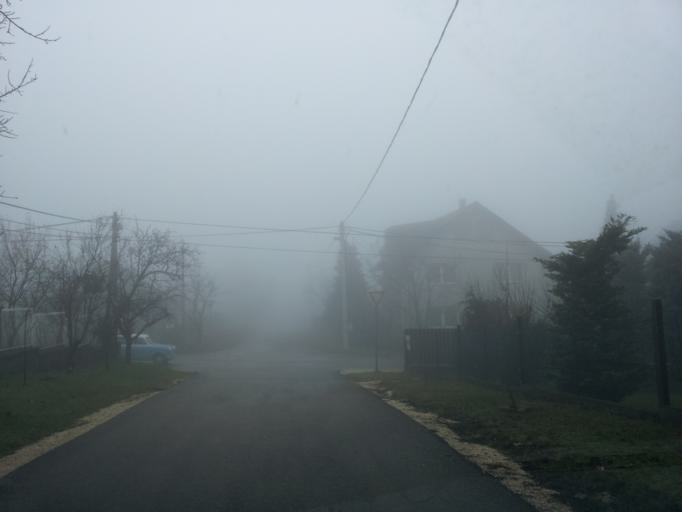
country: HU
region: Pest
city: Toeroekbalint
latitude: 47.4221
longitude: 18.8832
